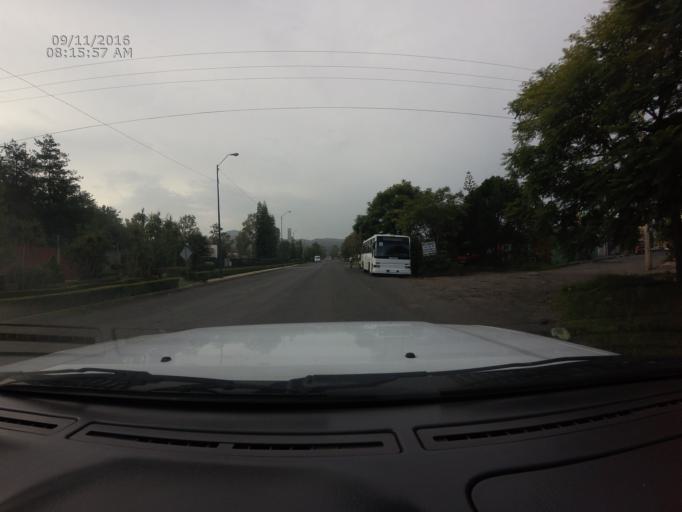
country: MX
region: Michoacan
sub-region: Morelia
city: Morelos
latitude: 19.6517
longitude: -101.2311
